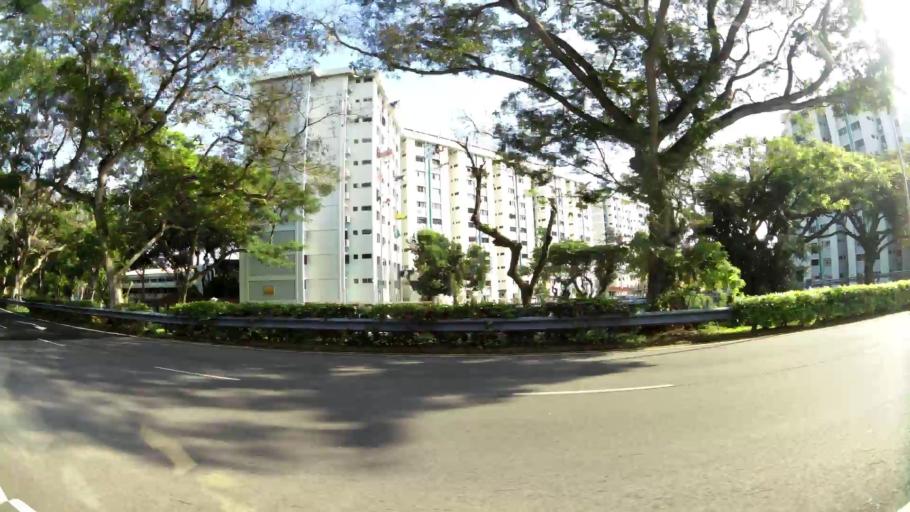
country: SG
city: Singapore
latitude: 1.3304
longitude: 103.9217
